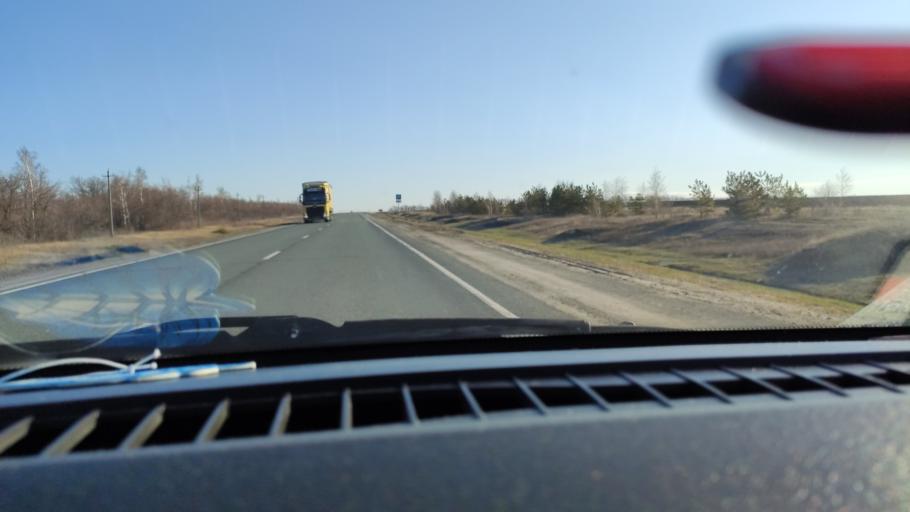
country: RU
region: Saratov
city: Alekseyevka
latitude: 52.2595
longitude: 47.9197
